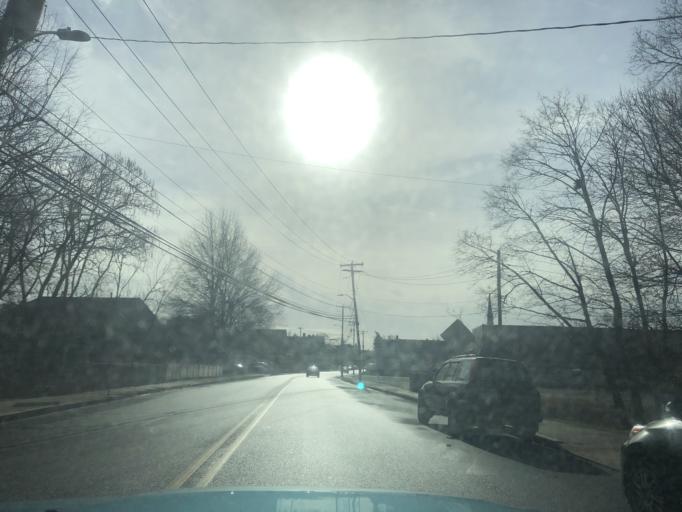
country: US
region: Pennsylvania
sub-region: Bucks County
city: Quakertown
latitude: 40.4452
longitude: -75.3338
